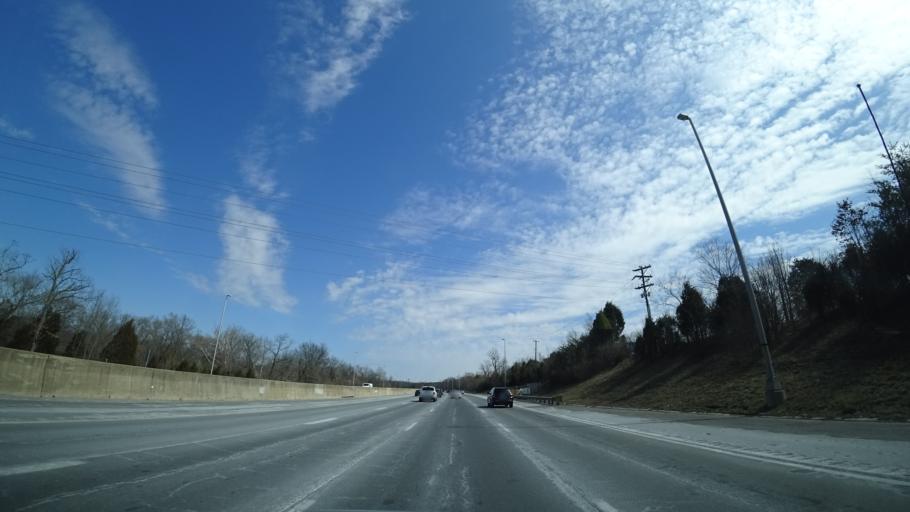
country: US
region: Virginia
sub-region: Prince William County
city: Yorkshire
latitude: 38.8186
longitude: -77.4682
